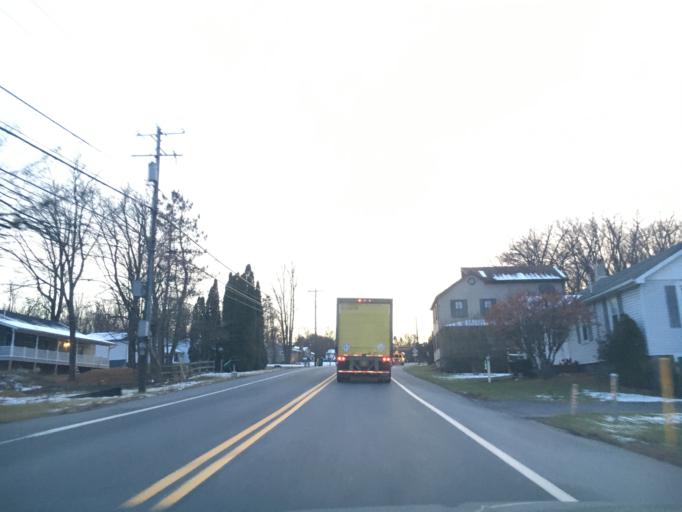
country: US
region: Pennsylvania
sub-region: Northampton County
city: Wind Gap
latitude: 40.8111
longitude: -75.3354
